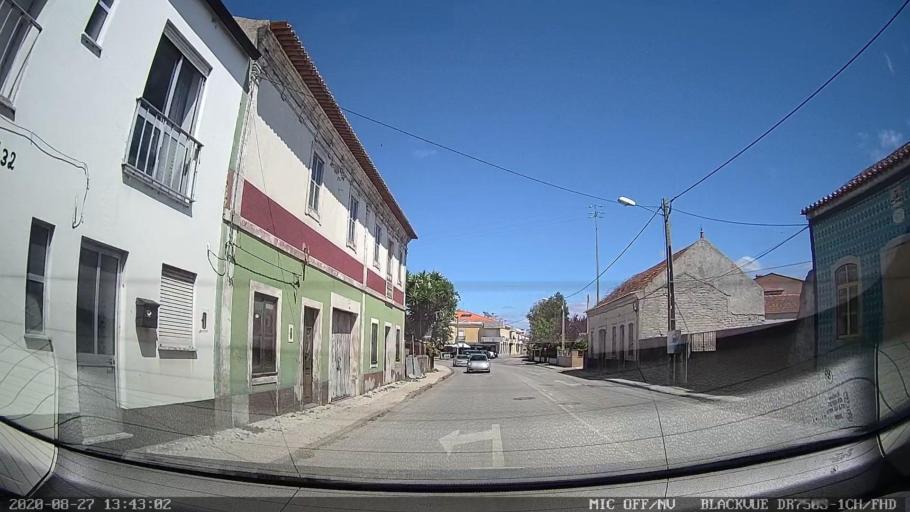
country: PT
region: Coimbra
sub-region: Mira
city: Mira
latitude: 40.4234
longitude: -8.7386
